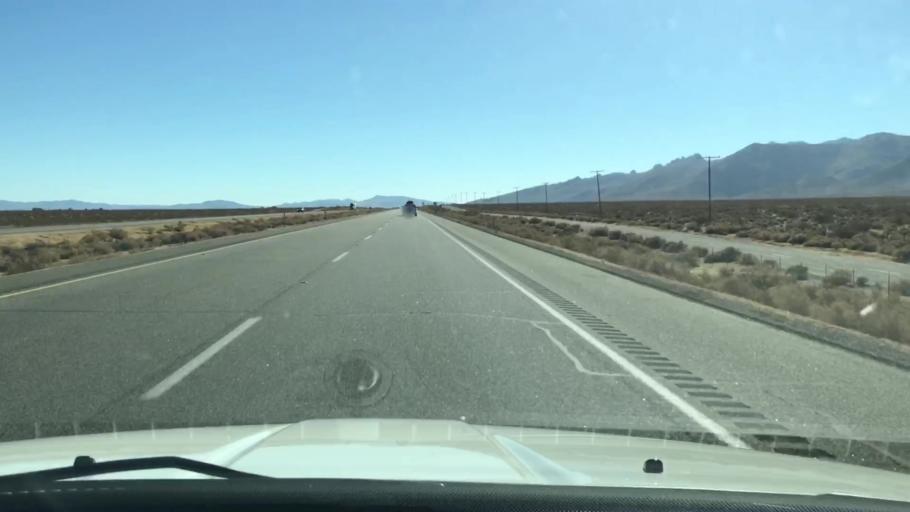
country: US
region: California
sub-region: Kern County
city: Inyokern
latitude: 35.7945
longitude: -117.8727
